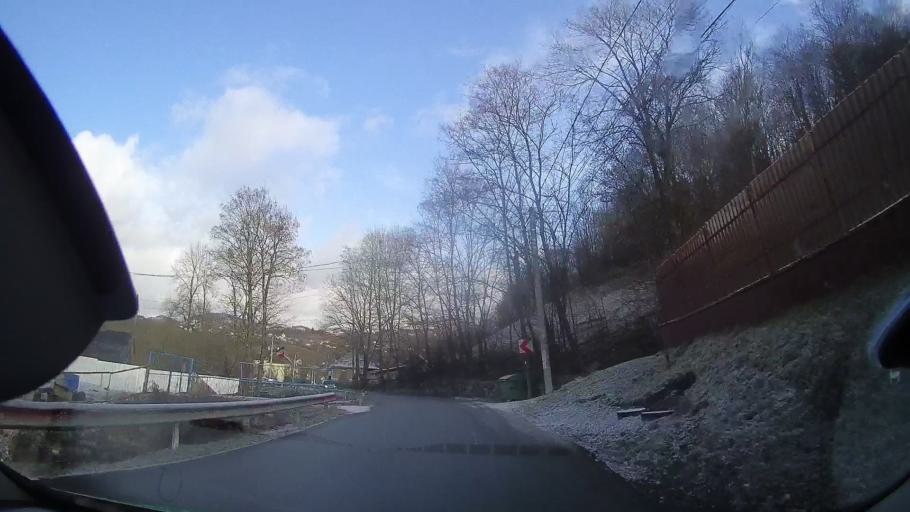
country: RO
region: Alba
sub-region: Comuna Sohodol
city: Sohodol
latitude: 46.3522
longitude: 23.0291
